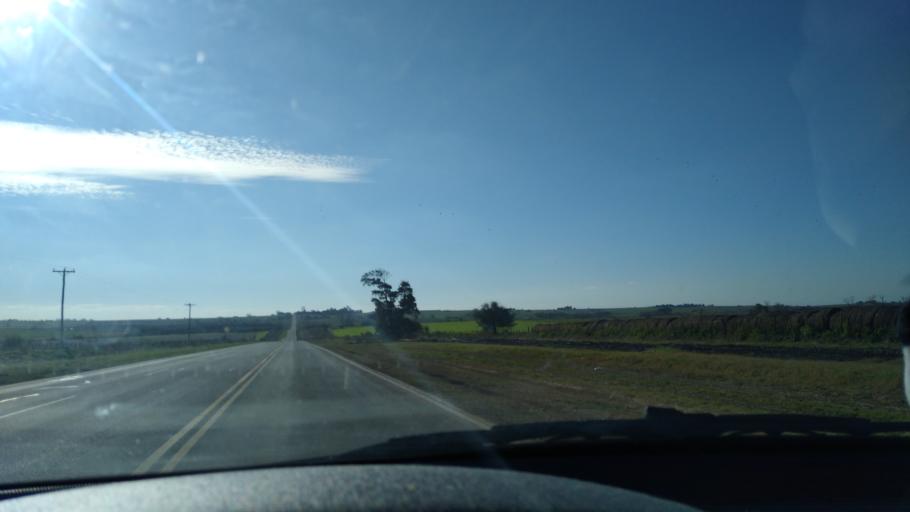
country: AR
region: Entre Rios
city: Aranguren
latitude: -32.3851
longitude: -60.3346
